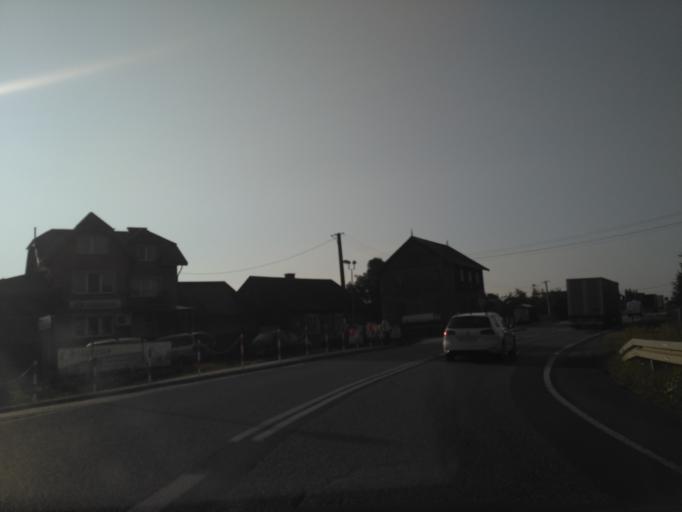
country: PL
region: Lublin Voivodeship
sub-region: Powiat krasnicki
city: Szastarka
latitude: 50.8251
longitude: 22.3136
